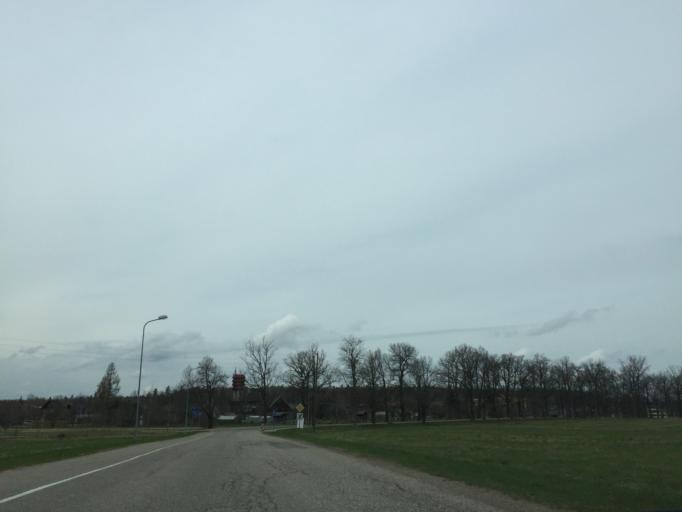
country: LV
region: Priekuli
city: Priekuli
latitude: 57.3476
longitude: 25.3323
